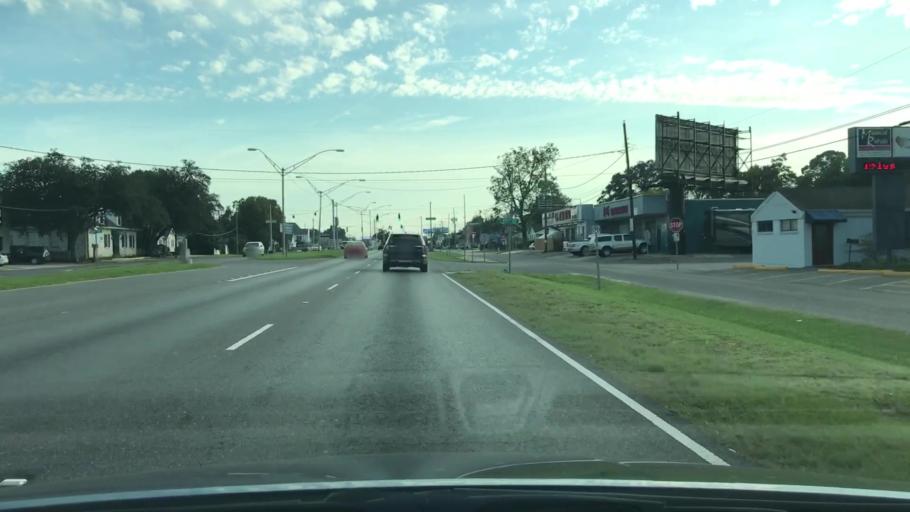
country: US
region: Louisiana
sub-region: Jefferson Parish
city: Metairie
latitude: 29.9834
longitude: -90.1561
